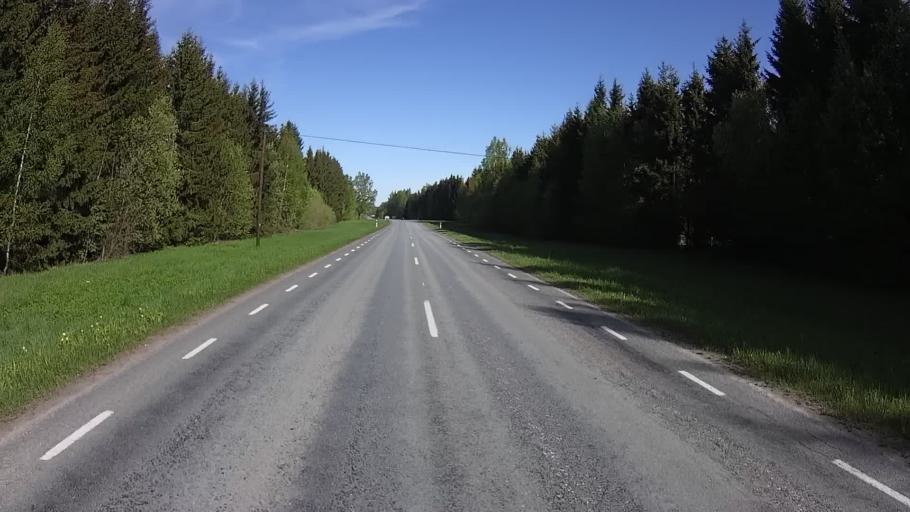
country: EE
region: Polvamaa
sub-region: Polva linn
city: Polva
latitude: 58.2319
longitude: 27.0218
